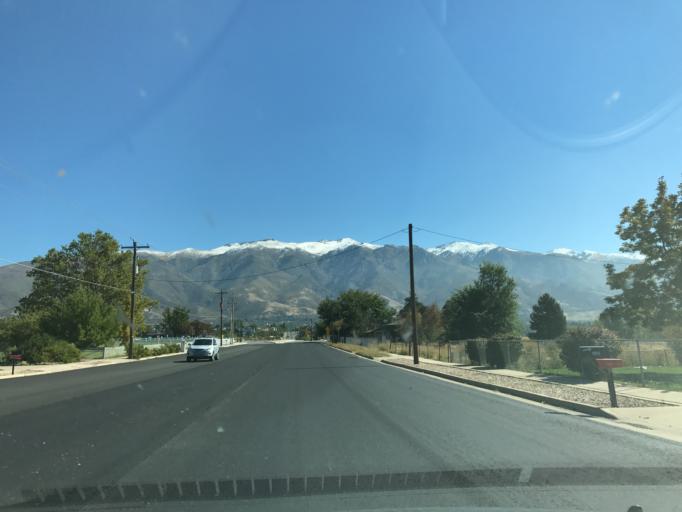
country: US
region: Utah
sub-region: Davis County
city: Layton
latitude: 41.0889
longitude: -111.9474
